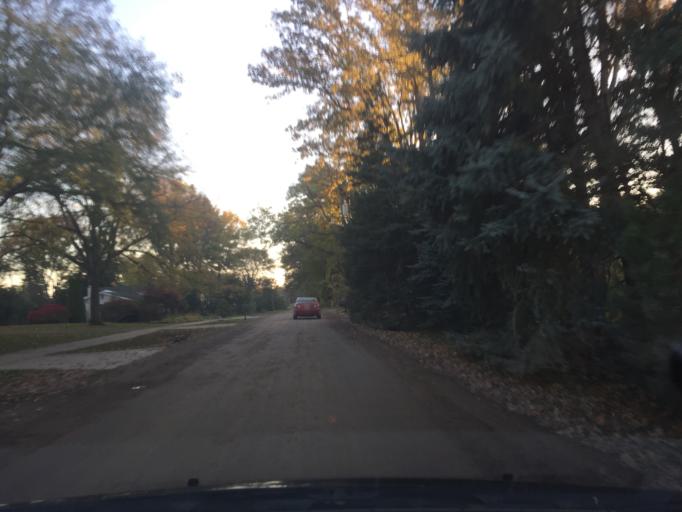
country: US
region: Michigan
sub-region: Oakland County
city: Franklin
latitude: 42.5632
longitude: -83.2949
